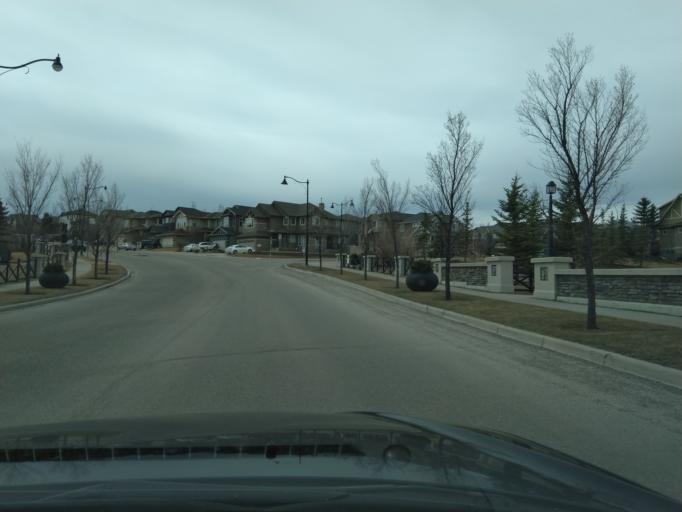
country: CA
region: Alberta
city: Calgary
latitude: 51.1651
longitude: -114.0825
